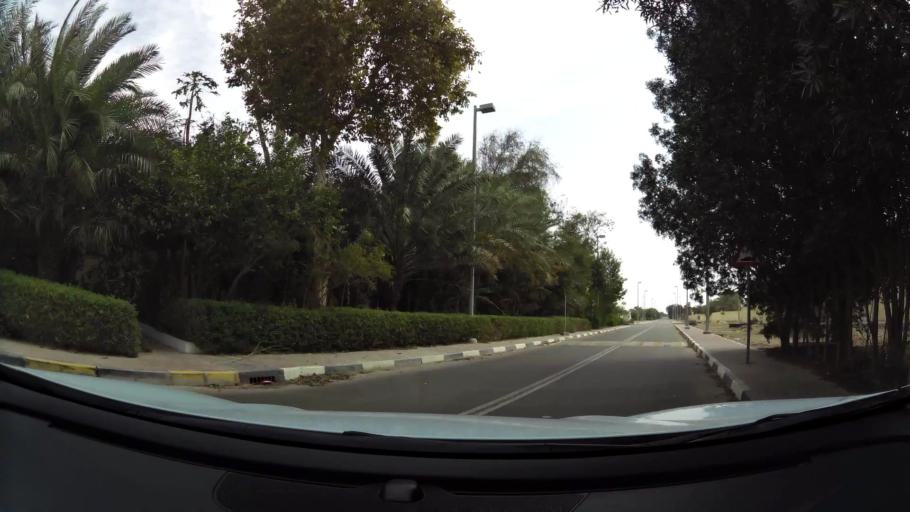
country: AE
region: Abu Dhabi
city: Abu Dhabi
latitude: 24.5227
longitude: 54.6777
